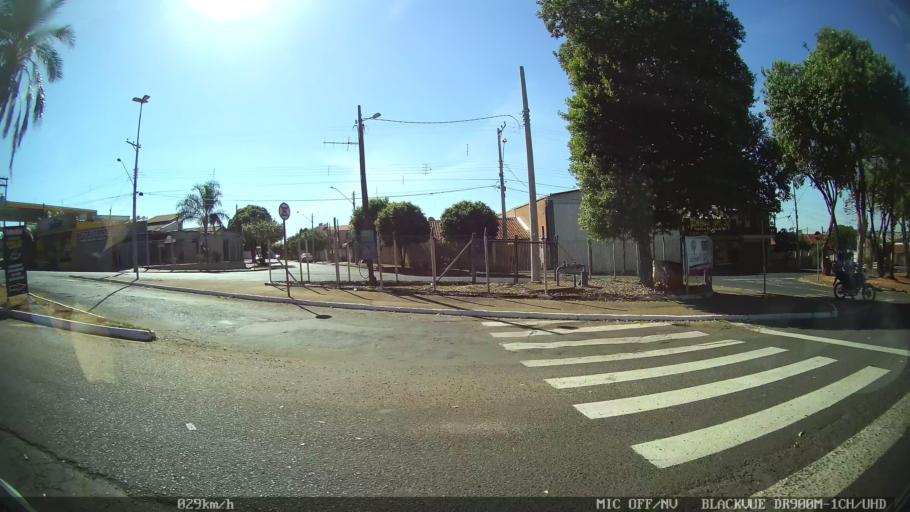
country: BR
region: Sao Paulo
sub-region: Olimpia
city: Olimpia
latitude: -20.7381
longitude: -48.8897
